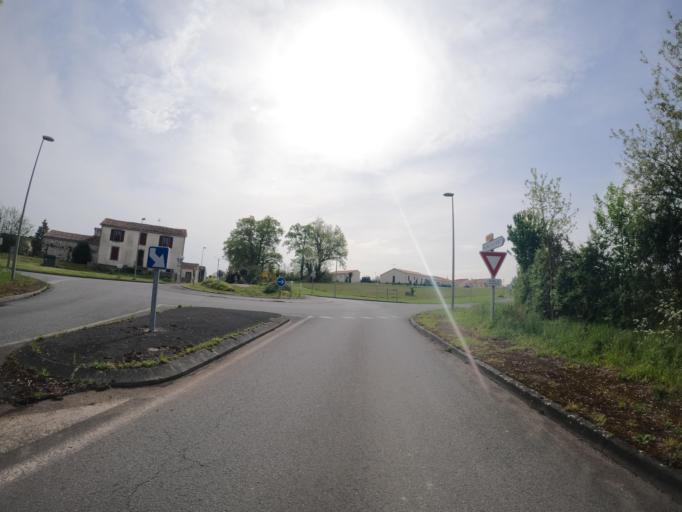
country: FR
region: Poitou-Charentes
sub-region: Departement des Deux-Sevres
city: La Chapelle-Saint-Laurent
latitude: 46.6952
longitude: -0.5042
